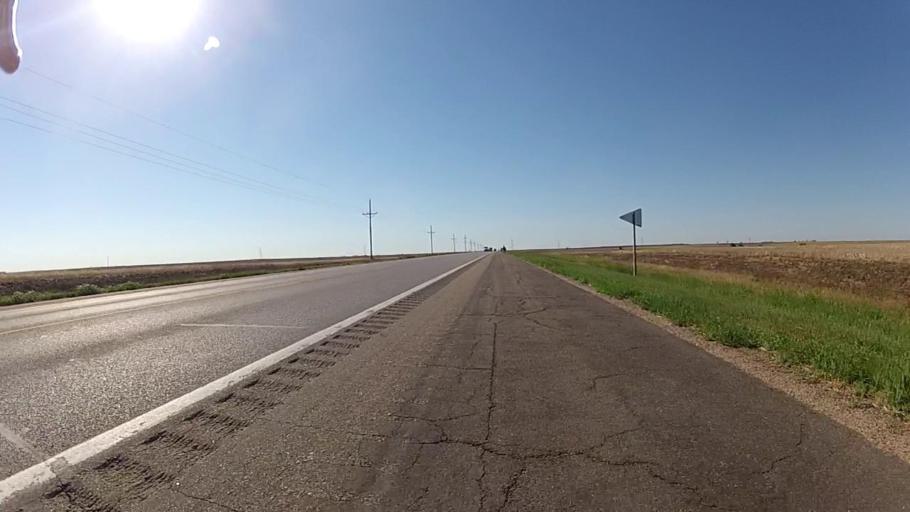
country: US
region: Kansas
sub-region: Ford County
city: Dodge City
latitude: 37.6083
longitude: -99.7111
